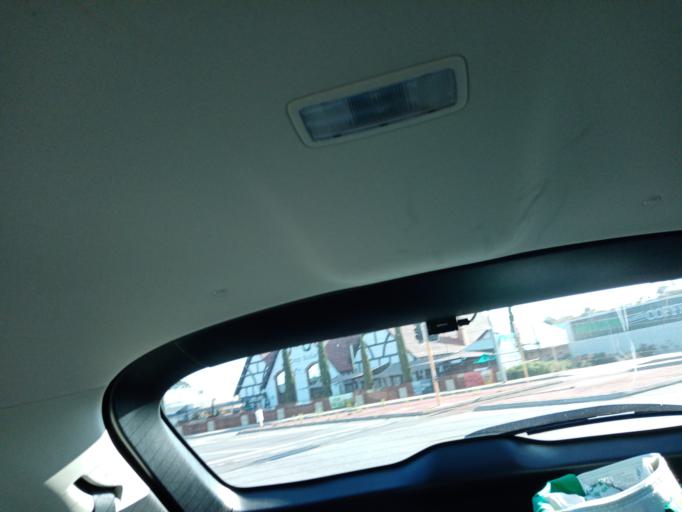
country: AU
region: Western Australia
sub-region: City of Cockburn
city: South Lake
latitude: -32.1270
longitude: 115.8423
